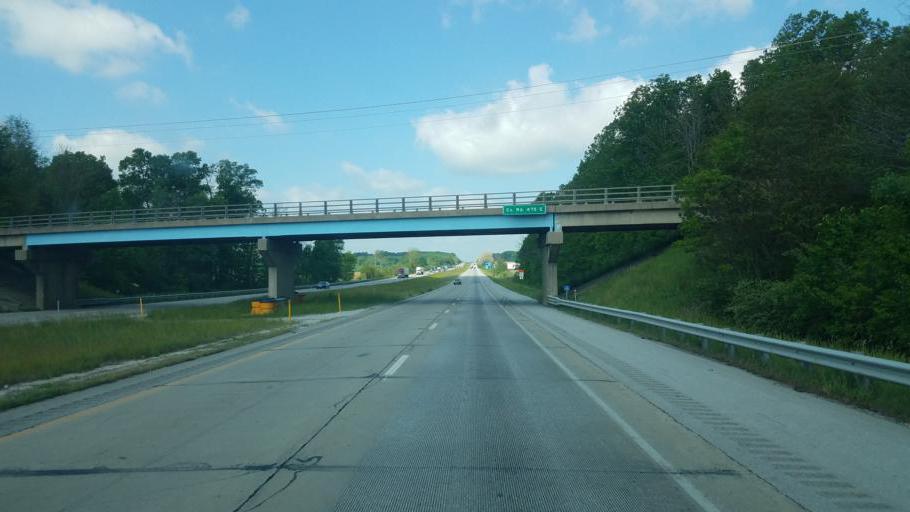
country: US
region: Indiana
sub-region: Putnam County
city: Cloverdale
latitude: 39.5381
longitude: -86.7667
